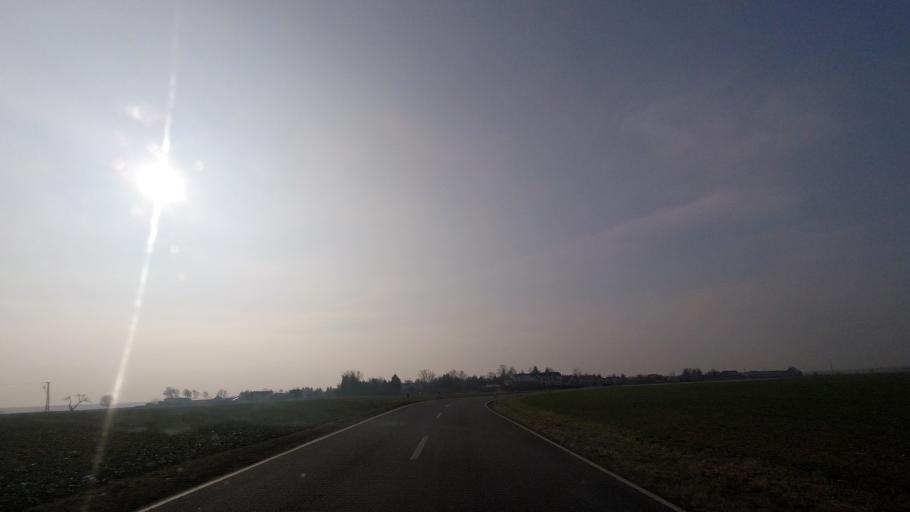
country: DE
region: Brandenburg
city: Juterbog
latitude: 51.8986
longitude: 13.0719
